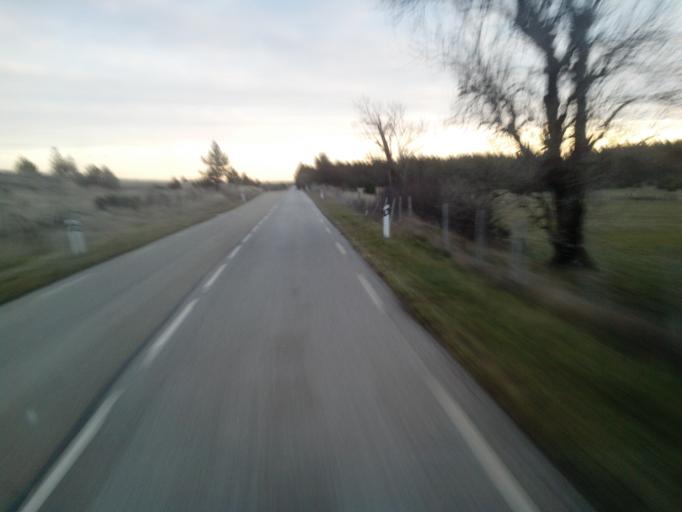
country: FR
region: Languedoc-Roussillon
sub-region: Departement de la Lozere
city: Florac
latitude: 44.2215
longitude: 3.6220
